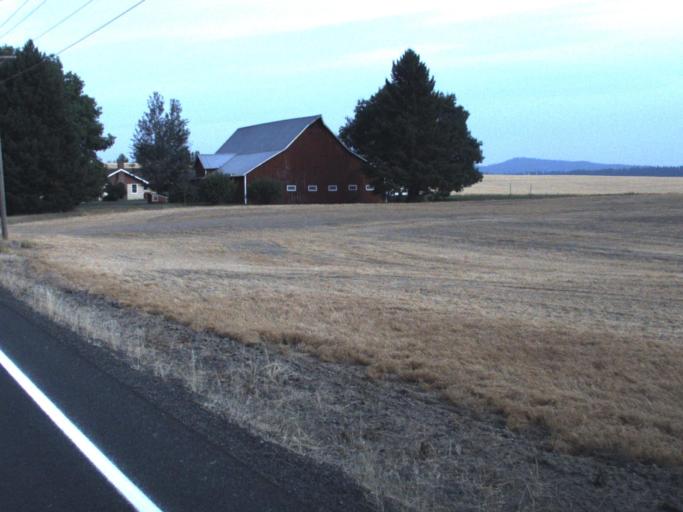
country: US
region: Washington
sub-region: Spokane County
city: Mead
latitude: 47.7875
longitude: -117.2950
